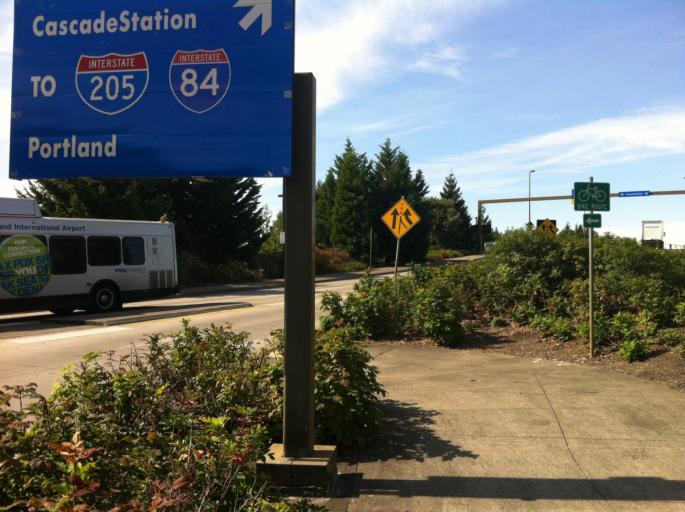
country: US
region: Washington
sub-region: Clark County
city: Orchards
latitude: 45.5777
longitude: -122.5599
